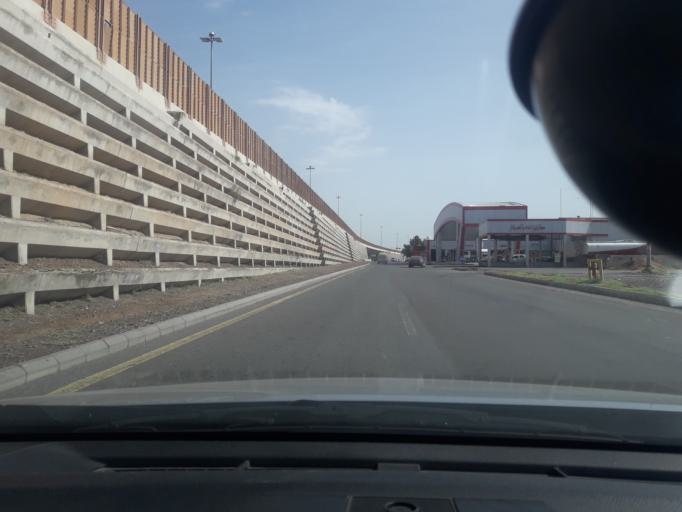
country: SA
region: Al Madinah al Munawwarah
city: Medina
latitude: 24.4501
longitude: 39.6647
